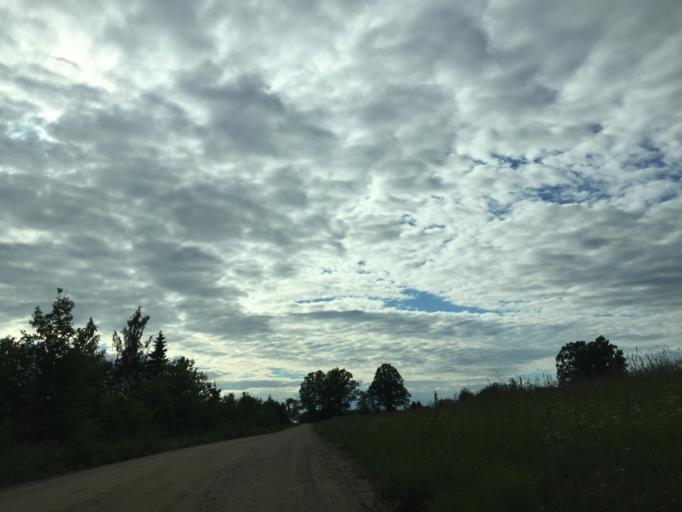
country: LV
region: Amatas Novads
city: Drabesi
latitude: 57.2445
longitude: 25.2016
